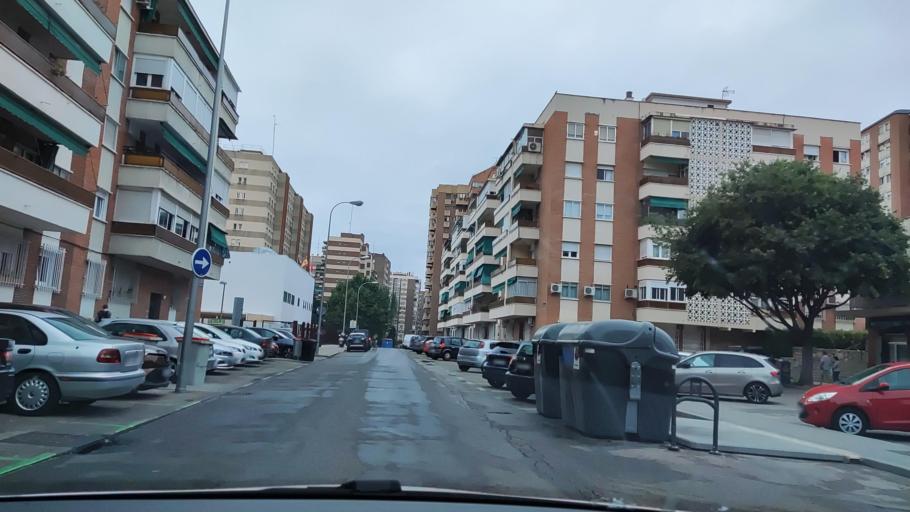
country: ES
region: Madrid
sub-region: Provincia de Madrid
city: Tetuan de las Victorias
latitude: 40.4865
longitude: -3.7006
